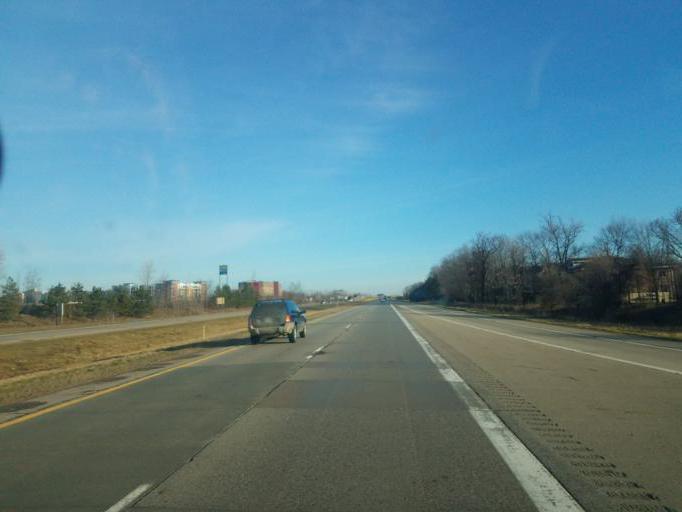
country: US
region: Michigan
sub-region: Ingham County
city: East Lansing
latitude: 42.7629
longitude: -84.5101
